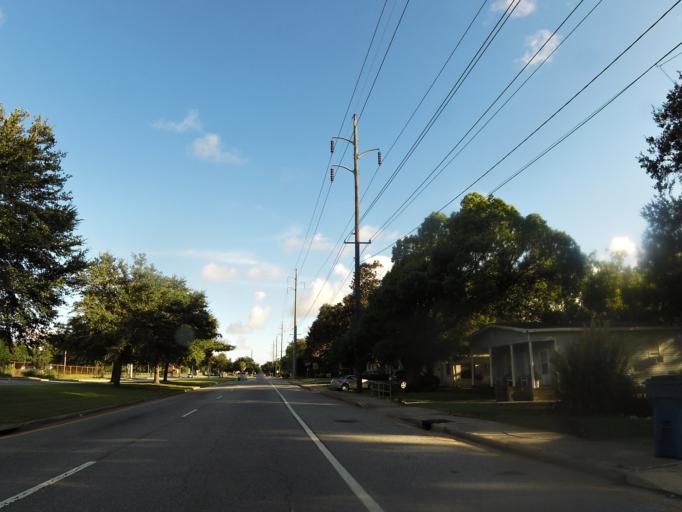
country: US
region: Georgia
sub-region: Glynn County
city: Brunswick
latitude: 31.1639
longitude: -81.4928
